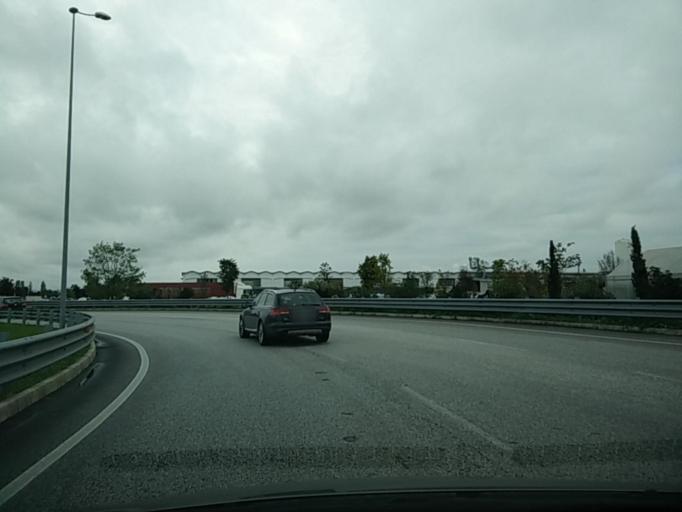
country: IT
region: Veneto
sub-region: Provincia di Padova
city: Galliera Veneta
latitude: 45.6613
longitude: 11.8051
